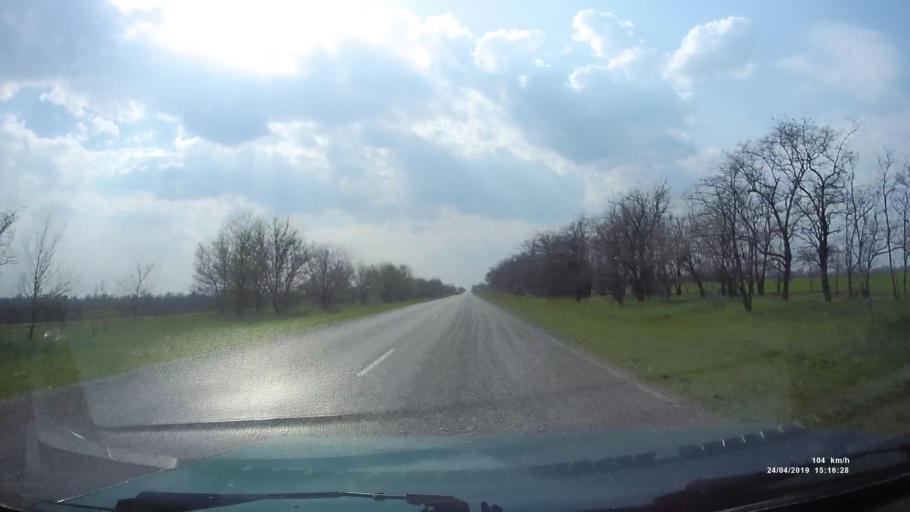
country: RU
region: Rostov
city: Remontnoye
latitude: 46.5465
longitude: 43.2123
